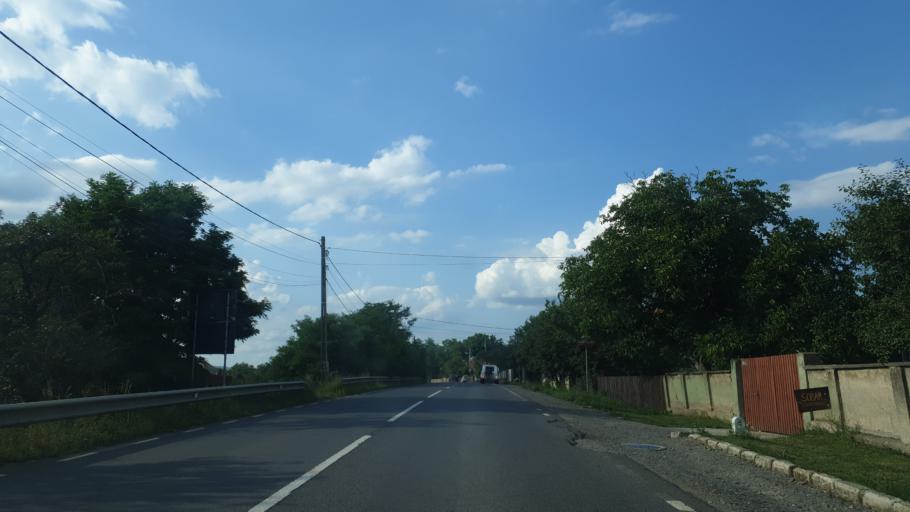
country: RO
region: Covasna
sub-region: Comuna Chichis
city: Chichis
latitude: 45.8098
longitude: 25.8004
